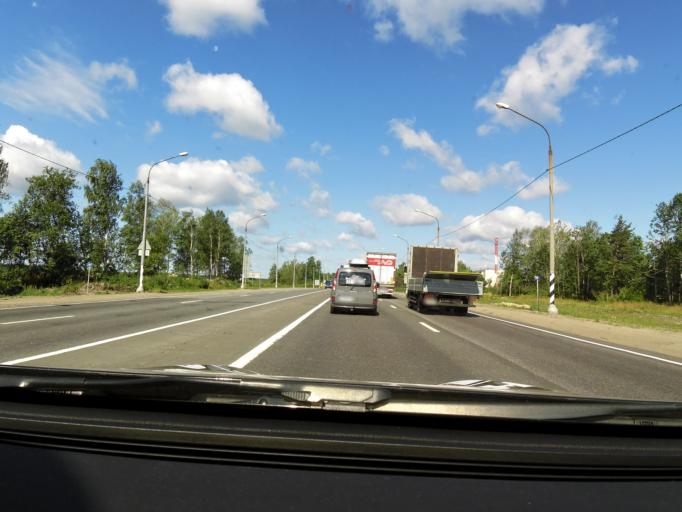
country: RU
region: Tverskaya
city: Tver
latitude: 56.8870
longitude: 35.7665
